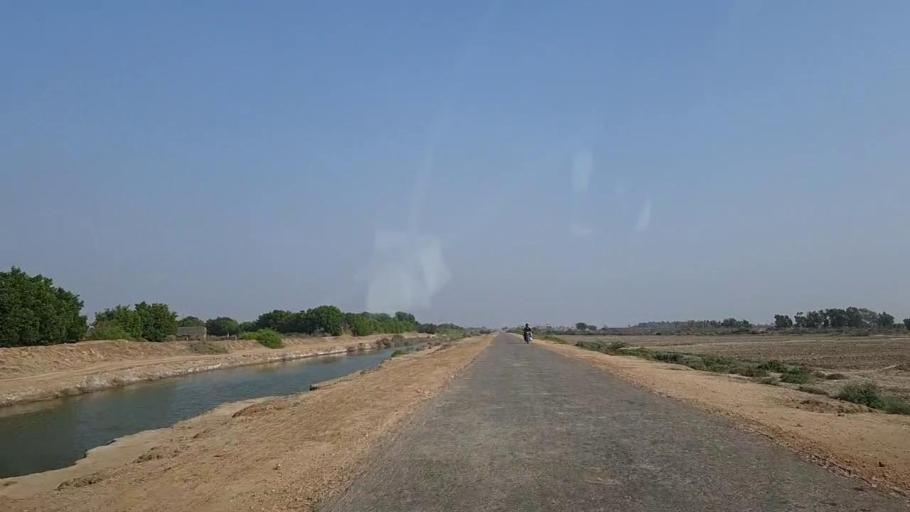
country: PK
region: Sindh
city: Mirpur Sakro
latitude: 24.6366
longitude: 67.6006
